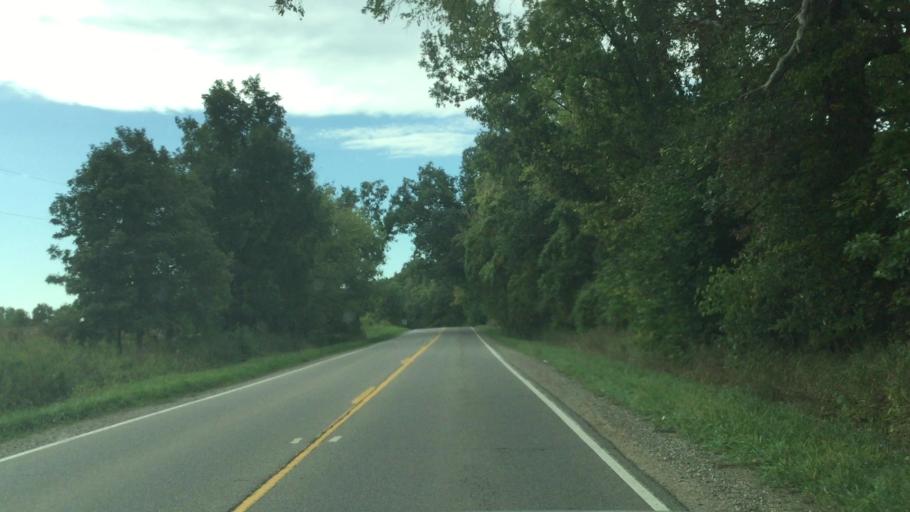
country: US
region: Michigan
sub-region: Genesee County
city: Argentine
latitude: 42.6996
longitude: -83.8404
